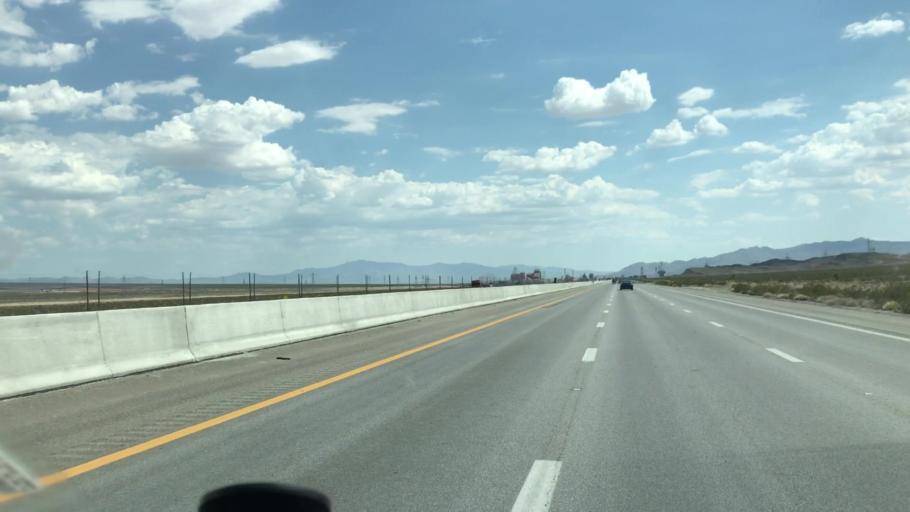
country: US
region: Nevada
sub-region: Clark County
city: Sandy Valley
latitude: 35.6436
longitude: -115.3832
